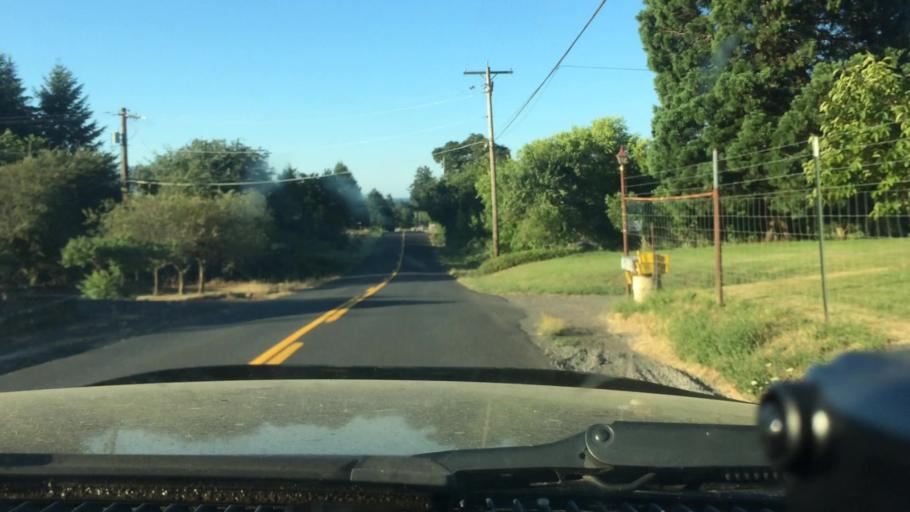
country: US
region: Oregon
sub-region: Yamhill County
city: Newberg
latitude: 45.3256
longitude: -122.9404
